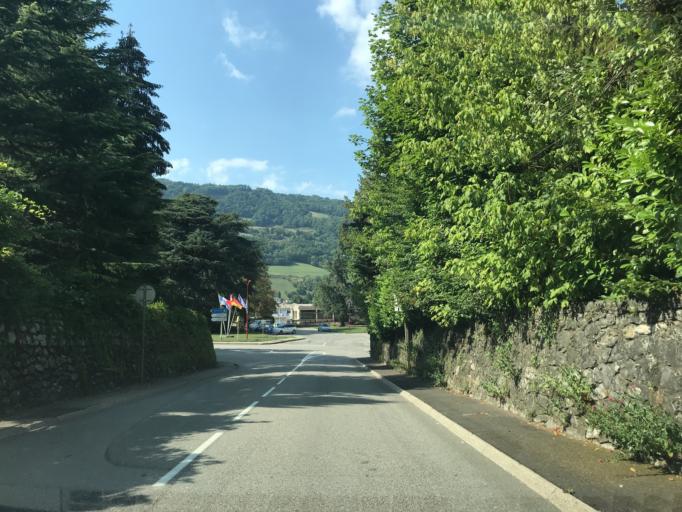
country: FR
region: Rhone-Alpes
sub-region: Departement de la Savoie
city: La Rochette
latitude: 45.4553
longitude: 6.1173
